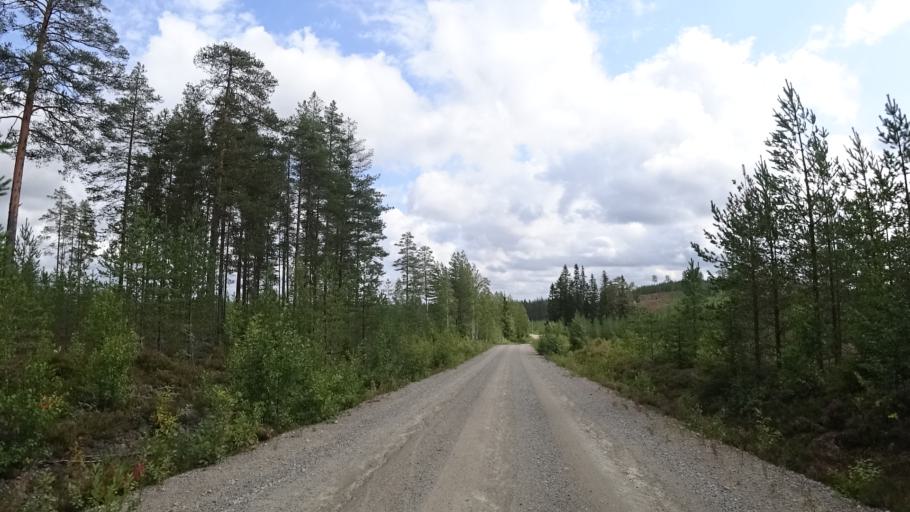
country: FI
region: North Karelia
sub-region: Joensuu
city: Ilomantsi
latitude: 62.9275
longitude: 31.3744
